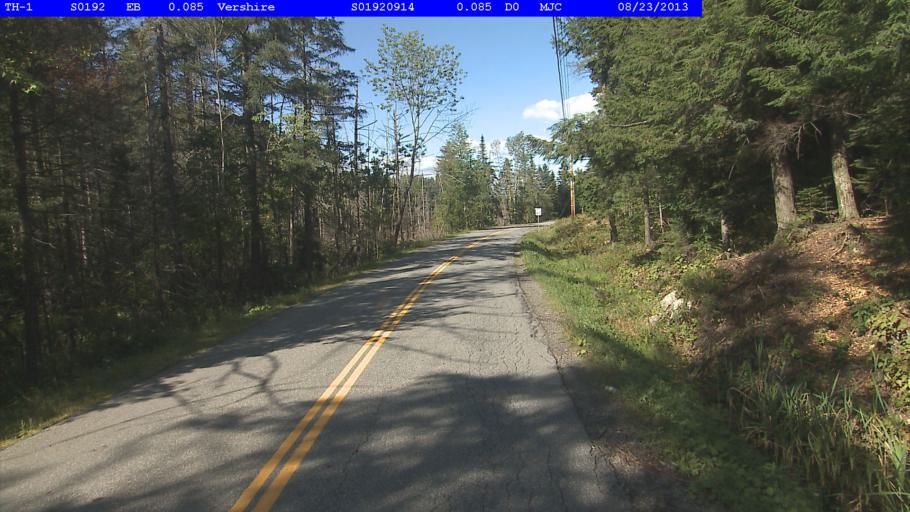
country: US
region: Vermont
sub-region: Orange County
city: Chelsea
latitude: 43.9888
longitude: -72.3688
